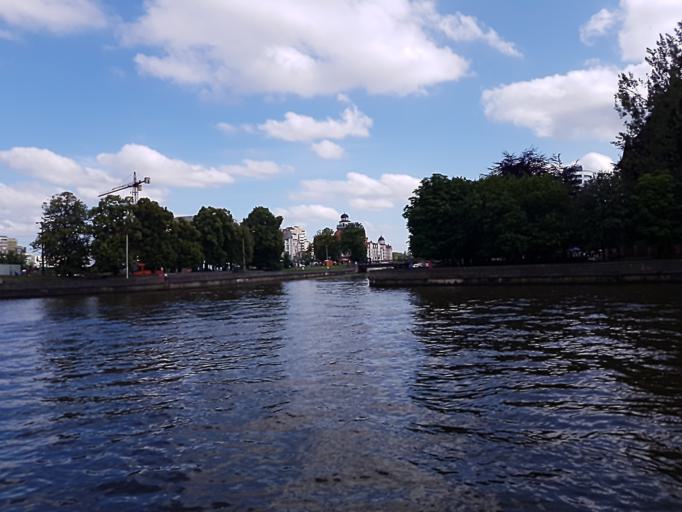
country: RU
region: Kaliningrad
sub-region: Gorod Kaliningrad
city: Kaliningrad
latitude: 54.7073
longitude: 20.5132
